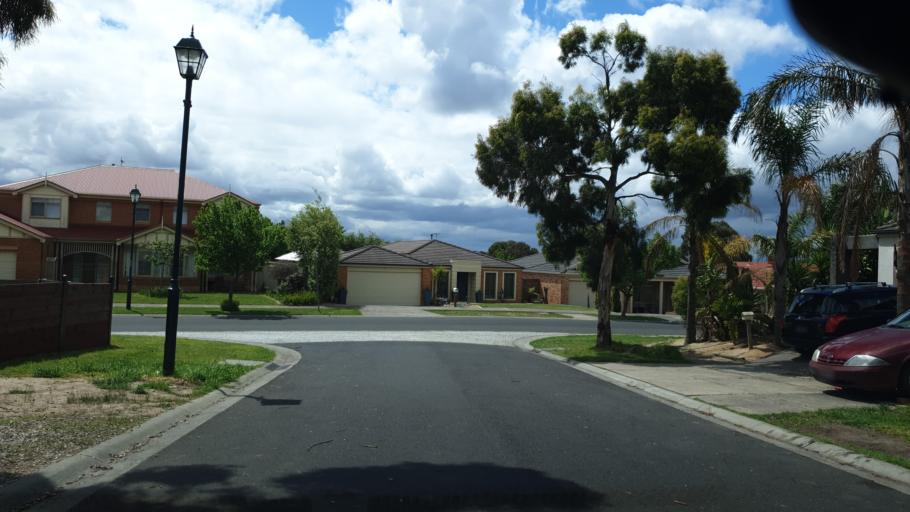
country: AU
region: Victoria
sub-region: Casey
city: Cranbourne East
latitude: -38.1049
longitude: 145.2999
